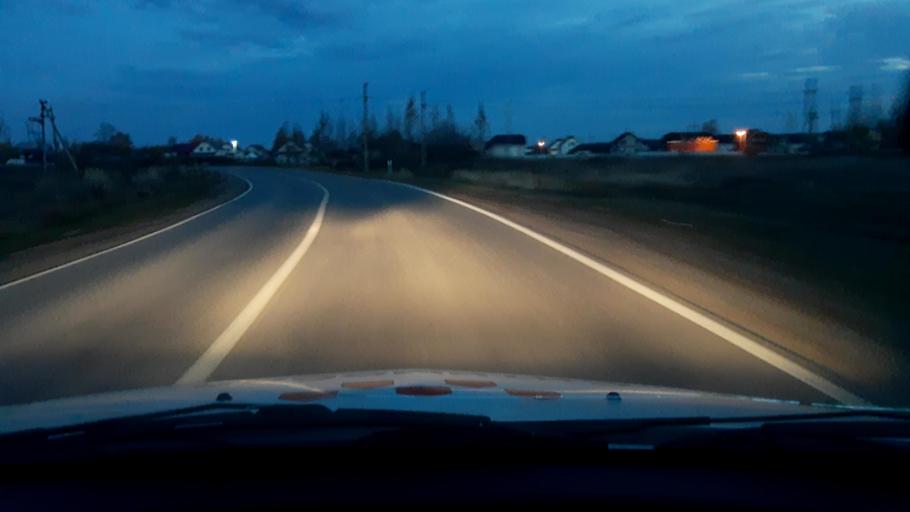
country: RU
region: Bashkortostan
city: Kabakovo
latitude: 54.7431
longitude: 56.2022
